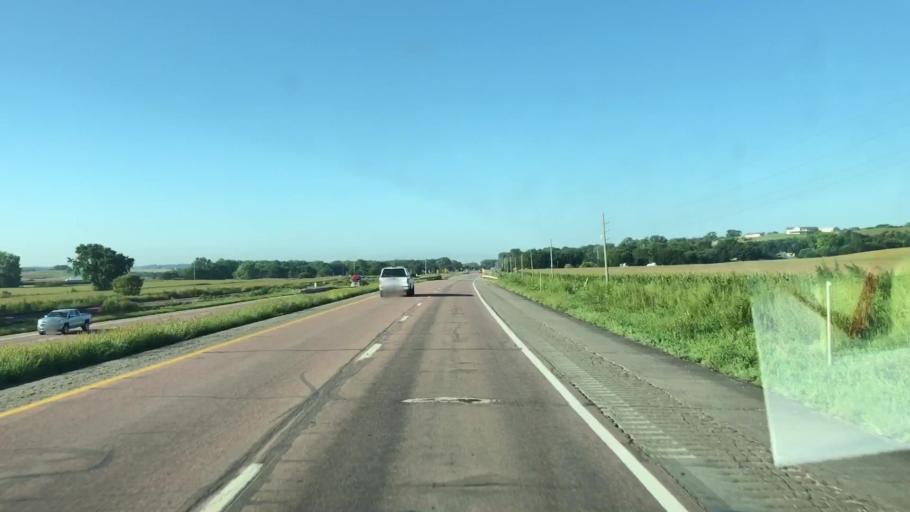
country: US
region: Iowa
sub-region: Woodbury County
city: Sioux City
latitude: 42.5822
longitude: -96.3117
